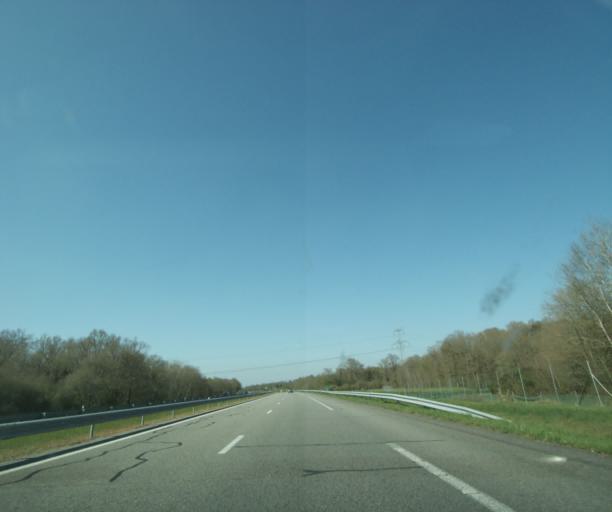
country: FR
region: Centre
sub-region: Departement du Loiret
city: Nogent-sur-Vernisson
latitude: 47.7607
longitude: 2.7185
